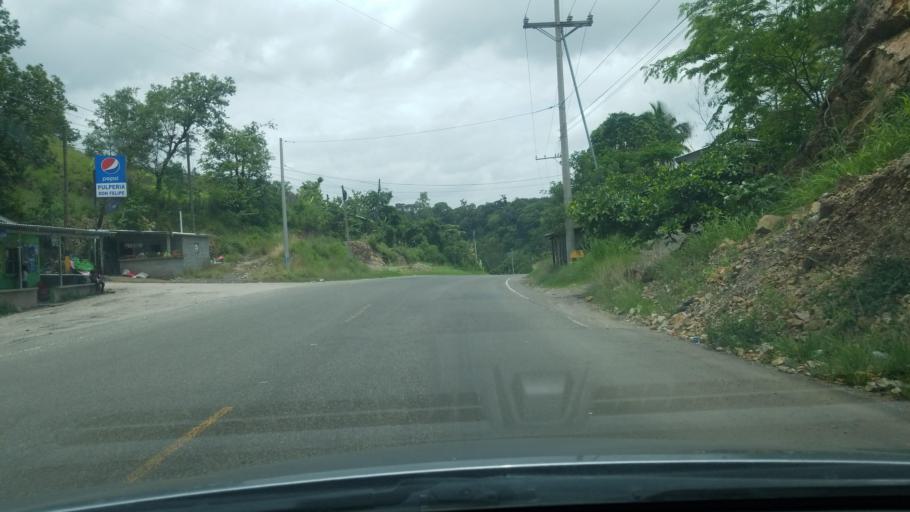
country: HN
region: Copan
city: Cucuyagua
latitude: 14.6714
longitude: -88.8404
